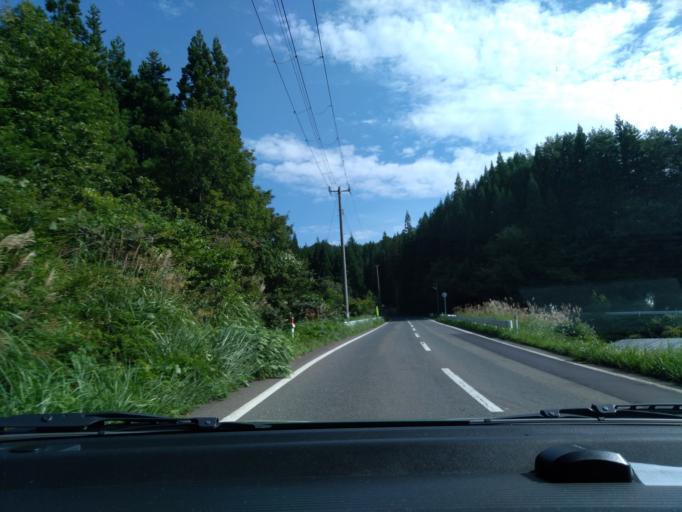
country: JP
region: Iwate
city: Shizukuishi
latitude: 39.6413
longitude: 141.0046
